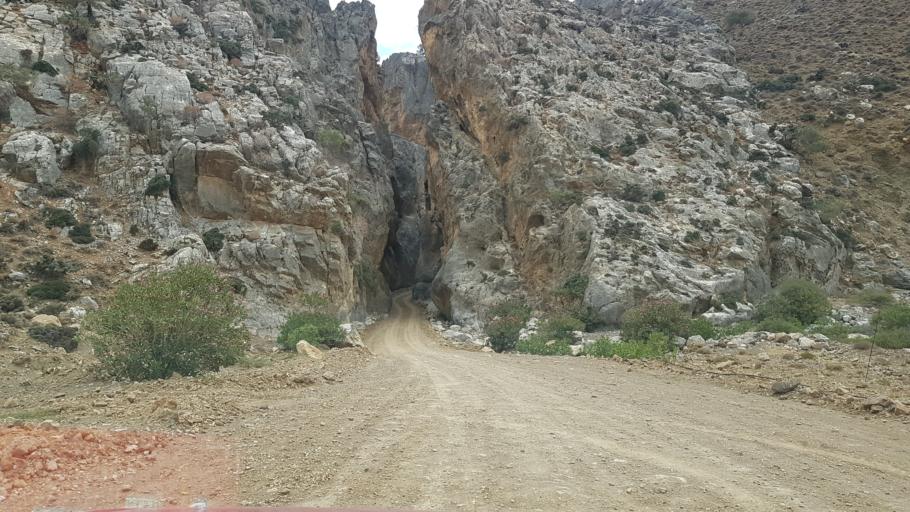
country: GR
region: Crete
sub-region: Nomos Irakleiou
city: Agioi Deka
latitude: 34.9435
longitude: 24.9854
